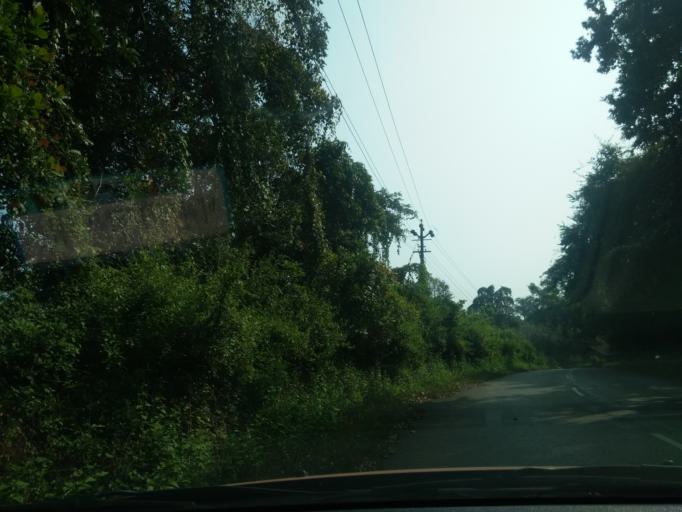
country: IN
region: Goa
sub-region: North Goa
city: Valpoy
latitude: 15.4827
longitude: 74.1357
